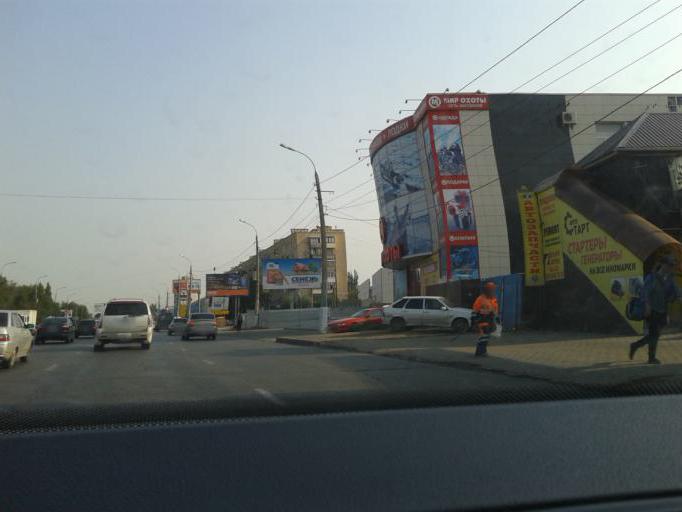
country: RU
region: Volgograd
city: Volgograd
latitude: 48.6728
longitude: 44.4432
